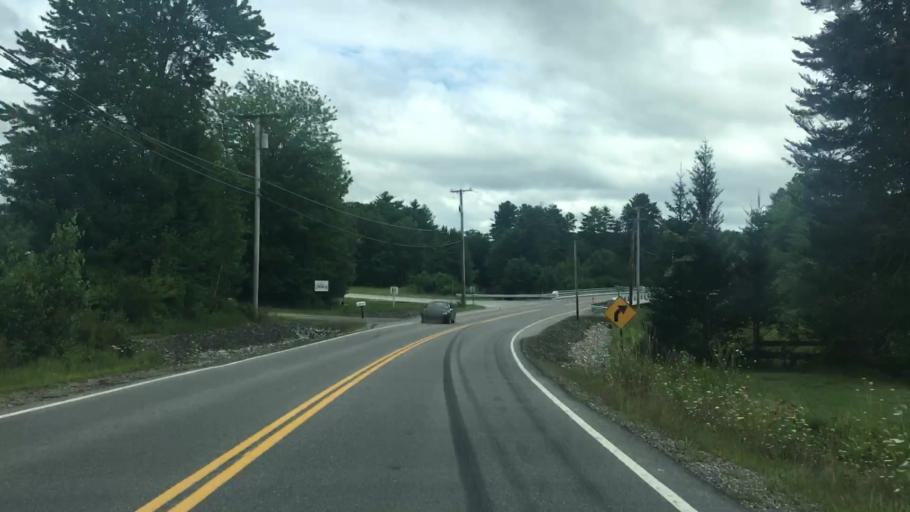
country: US
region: Maine
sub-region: York County
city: Lake Arrowhead
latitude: 43.6541
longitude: -70.7611
